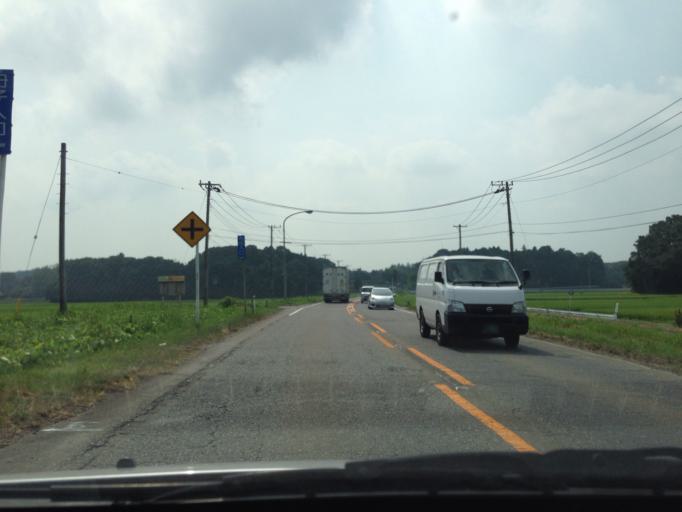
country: JP
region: Ibaraki
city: Inashiki
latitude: 36.0189
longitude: 140.2823
